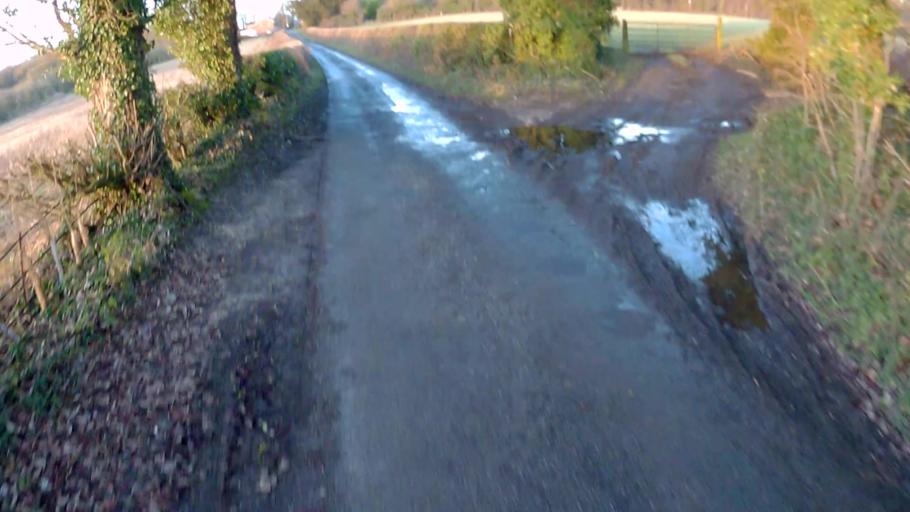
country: GB
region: England
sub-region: Hampshire
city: Overton
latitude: 51.2110
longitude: -1.2454
